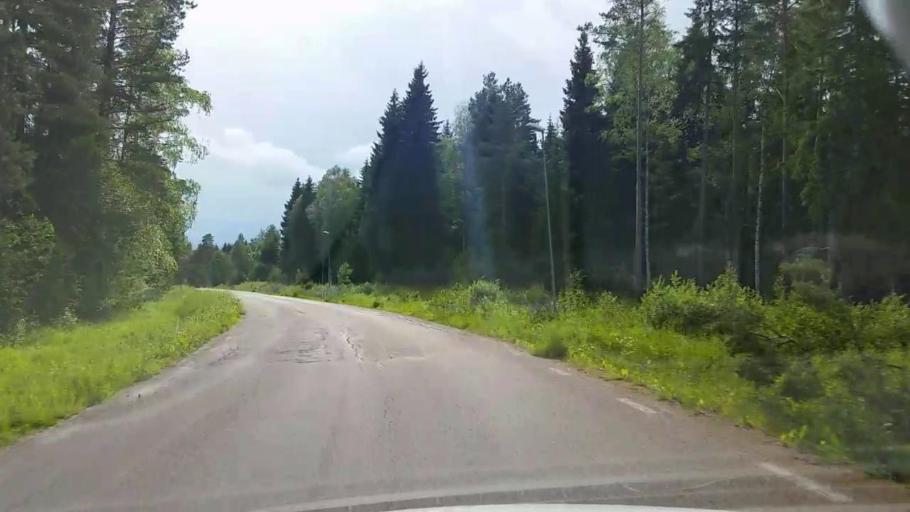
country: SE
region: Dalarna
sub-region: Smedjebackens Kommun
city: Smedjebacken
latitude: 60.1821
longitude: 15.3161
